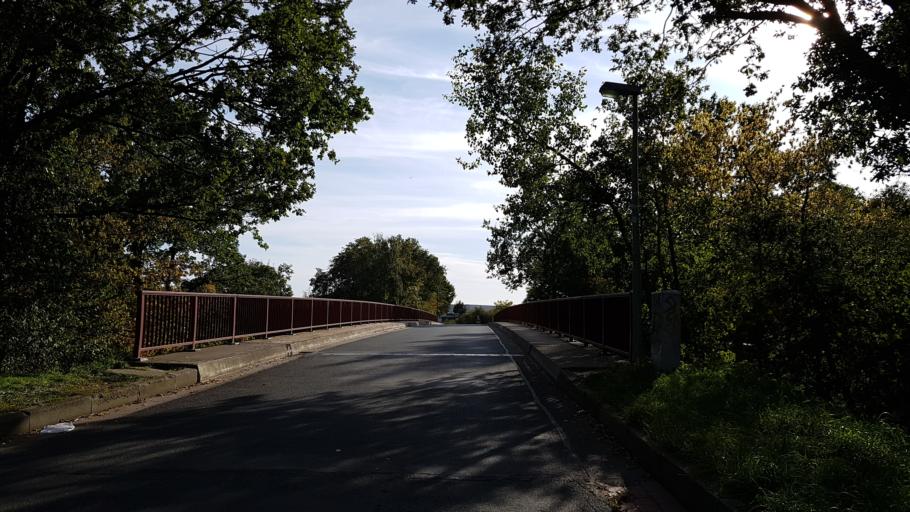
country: DE
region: Bremen
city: Bremen
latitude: 53.0426
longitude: 8.8860
